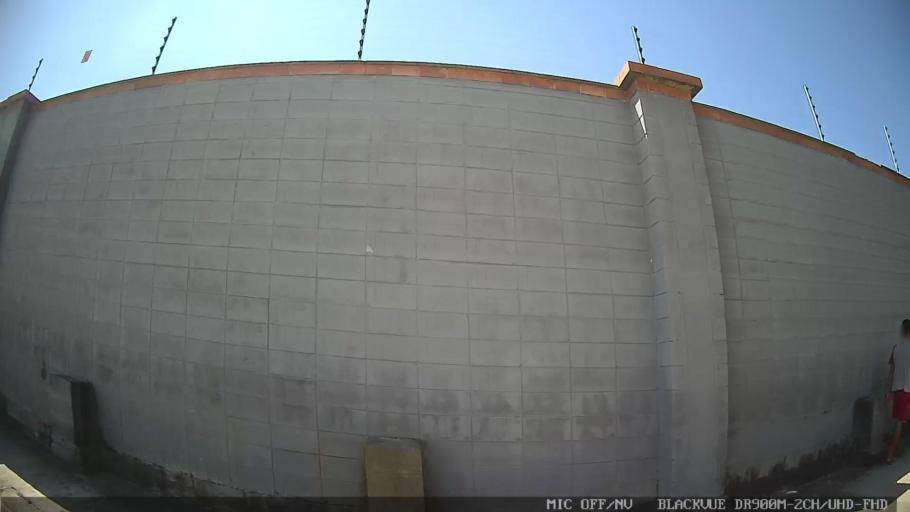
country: BR
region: Sao Paulo
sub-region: Peruibe
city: Peruibe
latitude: -24.3030
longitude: -46.9968
